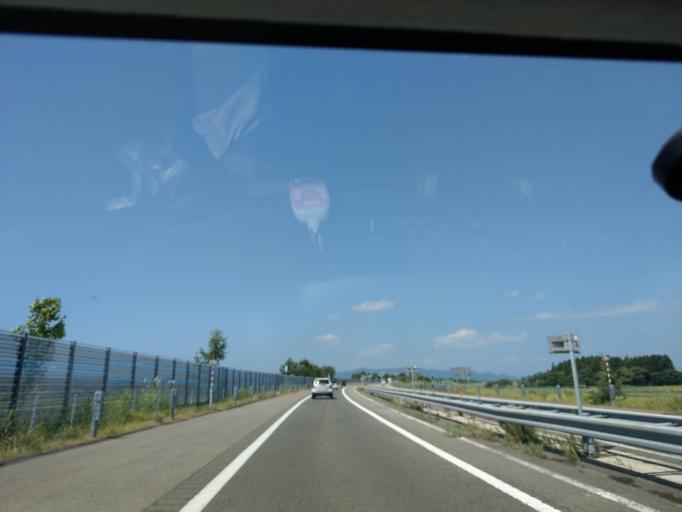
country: JP
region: Akita
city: Yokotemachi
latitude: 39.3575
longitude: 140.4917
